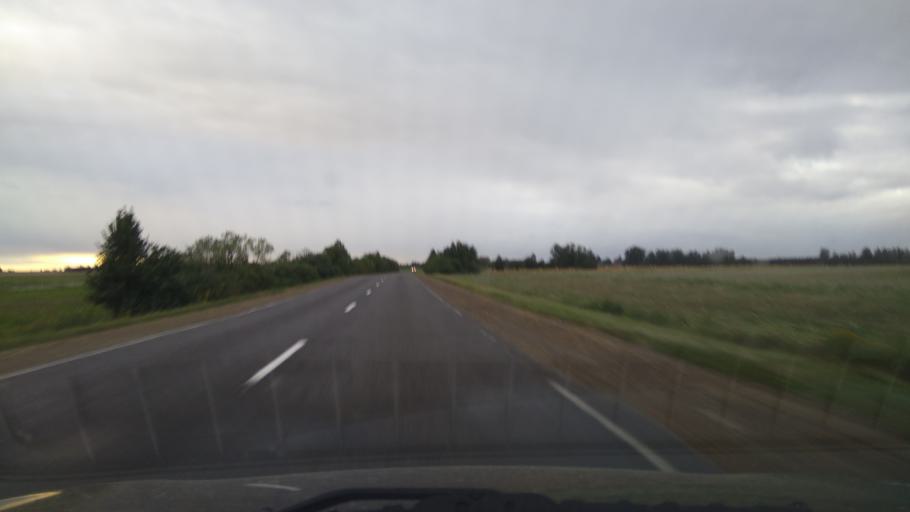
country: BY
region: Brest
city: Byaroza
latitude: 52.4445
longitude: 24.9737
